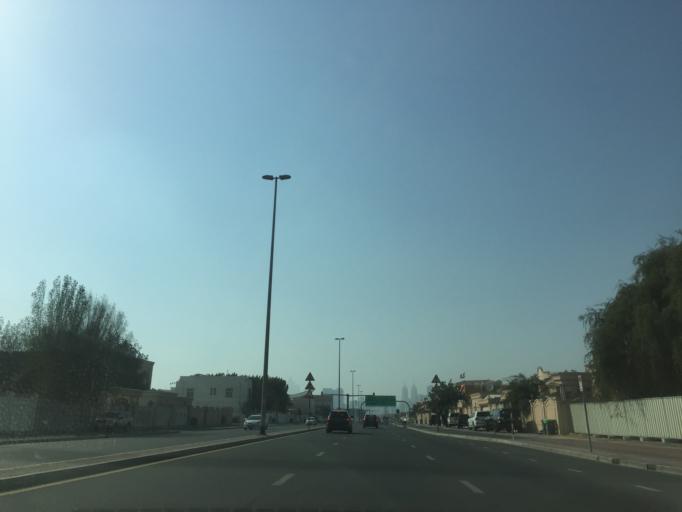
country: AE
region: Dubai
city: Dubai
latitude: 25.1005
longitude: 55.2102
